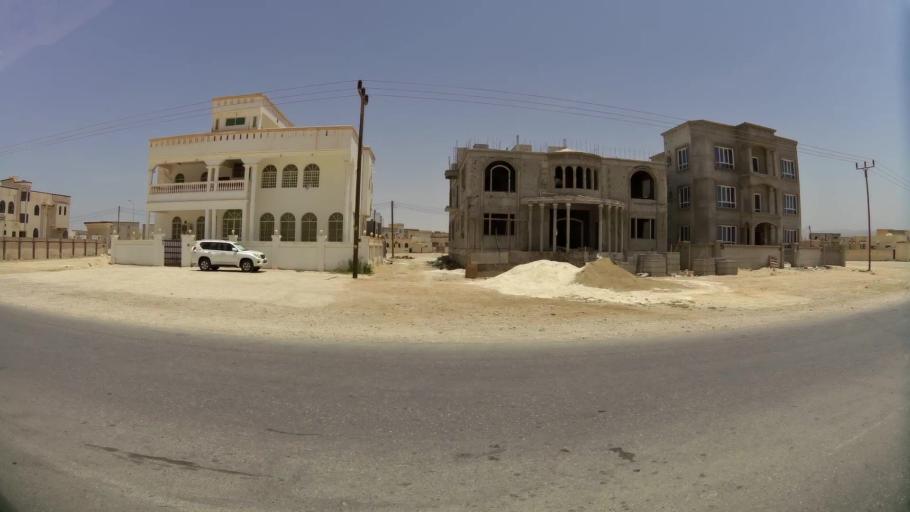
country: OM
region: Zufar
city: Salalah
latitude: 17.0809
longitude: 54.1591
